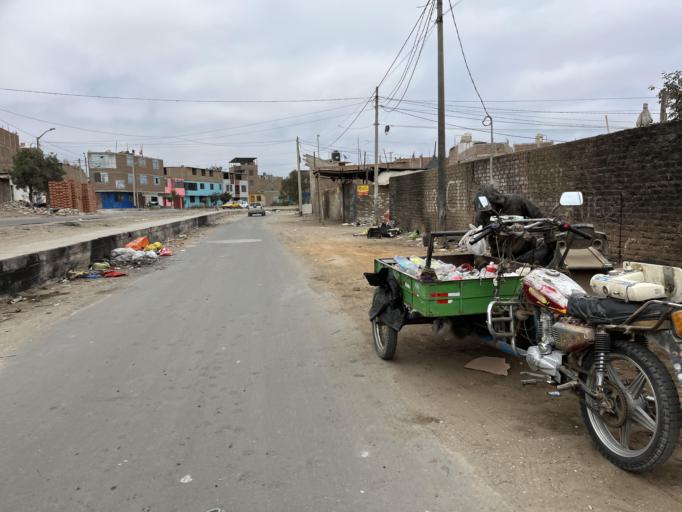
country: PE
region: La Libertad
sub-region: Provincia de Trujillo
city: La Esperanza
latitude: -8.0873
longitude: -79.0347
